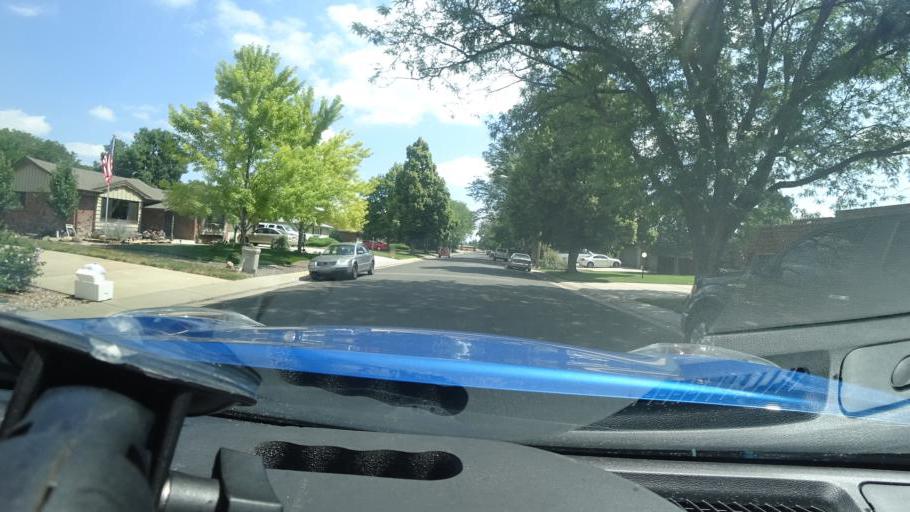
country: US
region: Colorado
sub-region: Adams County
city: Aurora
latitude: 39.7220
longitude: -104.8513
